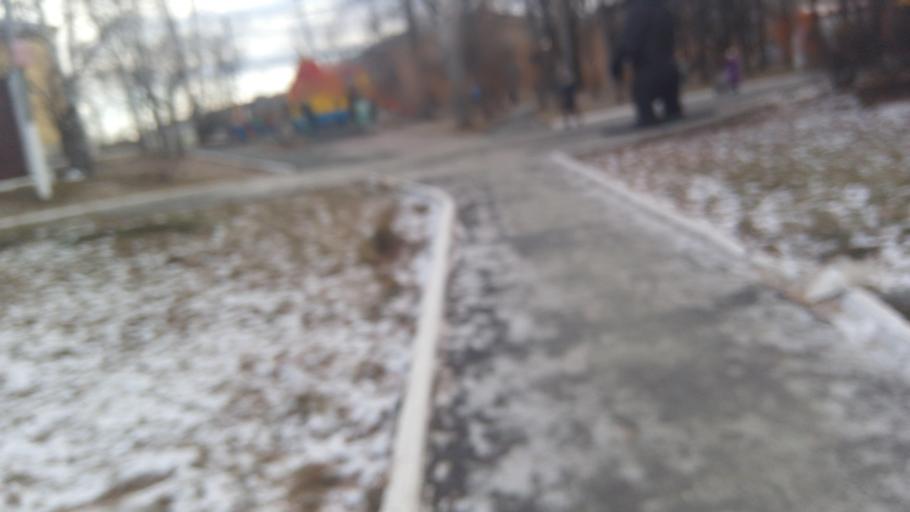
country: RU
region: Chelyabinsk
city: Zlatoust
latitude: 55.1086
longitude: 59.7202
